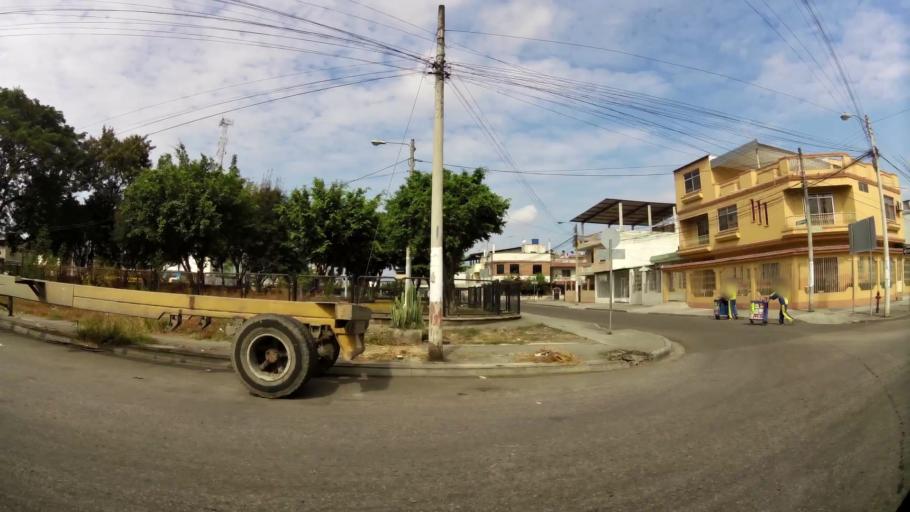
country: EC
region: Guayas
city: Guayaquil
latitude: -2.2596
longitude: -79.8929
